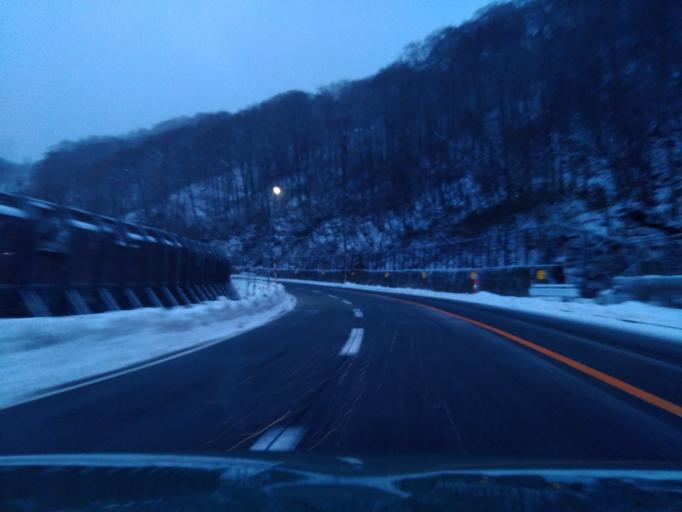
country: JP
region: Iwate
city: Shizukuishi
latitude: 39.7210
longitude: 140.8267
